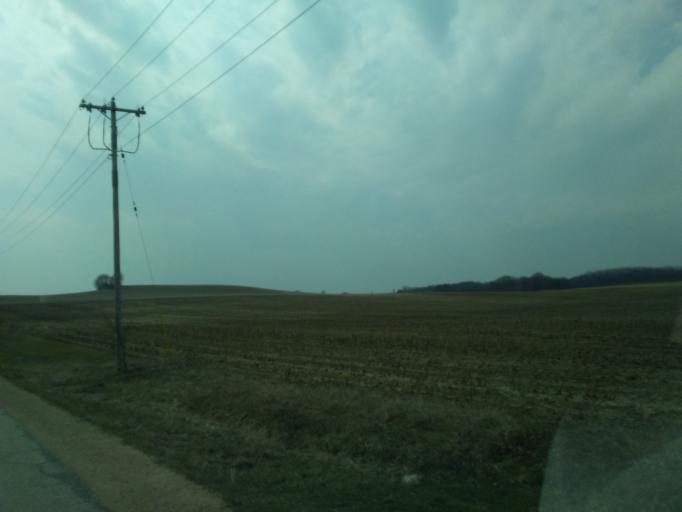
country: US
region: Wisconsin
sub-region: Dane County
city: Middleton
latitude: 43.1366
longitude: -89.4917
